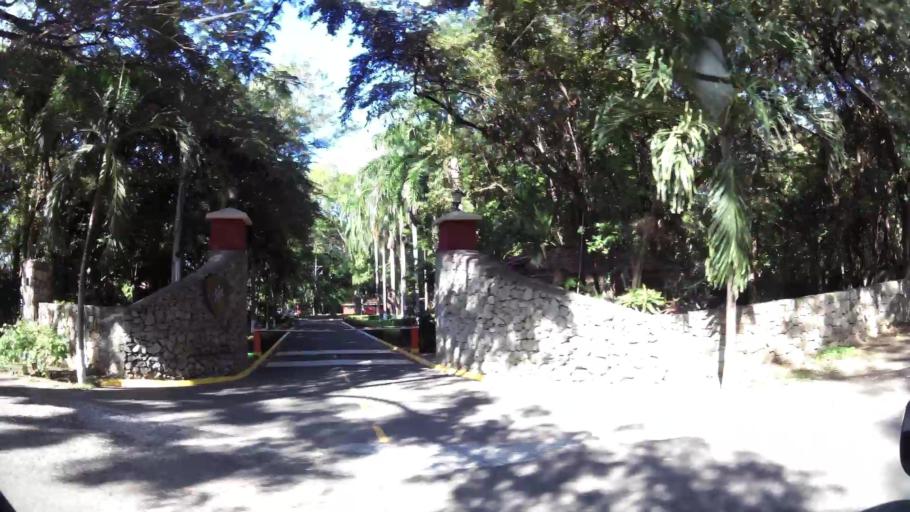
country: CR
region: Guanacaste
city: Sardinal
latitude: 10.5895
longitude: -85.6491
